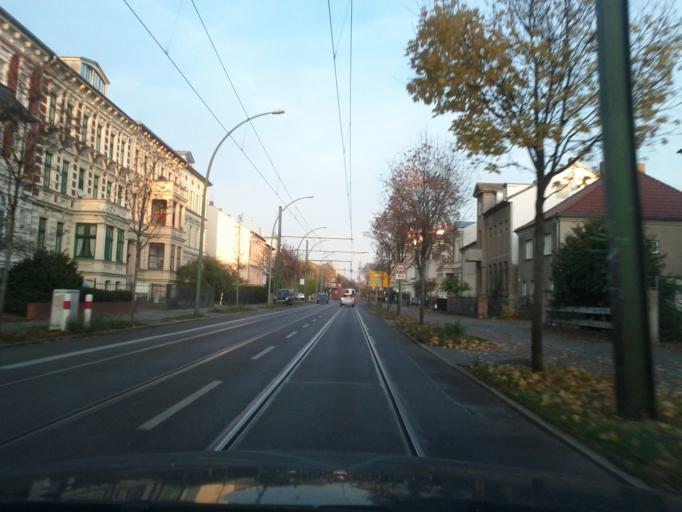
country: DE
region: Berlin
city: Friedrichshagen
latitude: 52.4564
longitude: 13.6225
